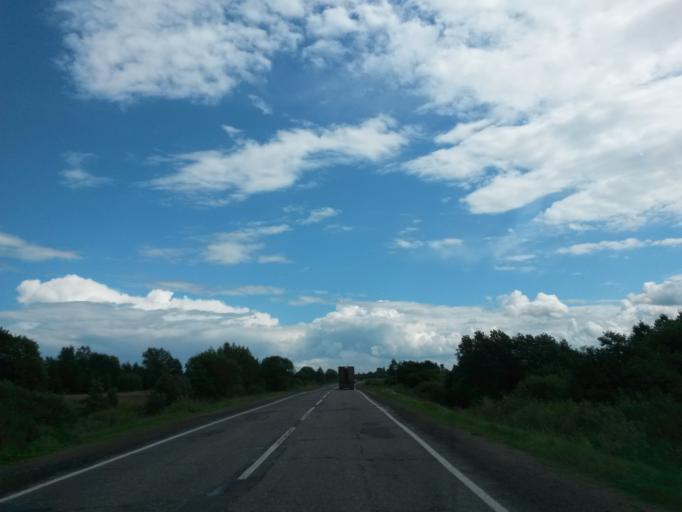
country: RU
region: Jaroslavl
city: Dubki
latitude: 57.2340
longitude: 40.2094
